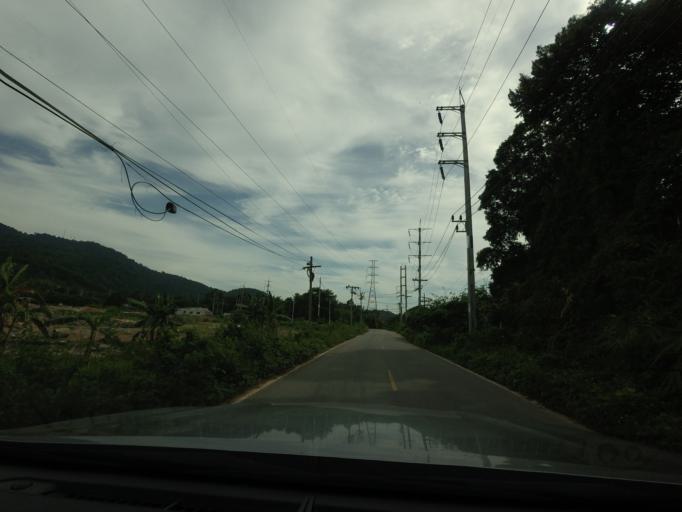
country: TH
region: Yala
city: Yala
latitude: 6.5056
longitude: 101.2882
